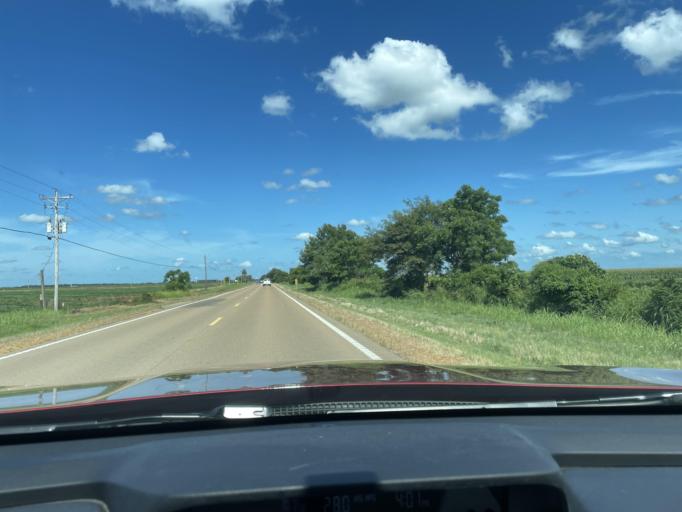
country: US
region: Mississippi
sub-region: Humphreys County
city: Belzoni
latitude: 33.1837
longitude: -90.5412
